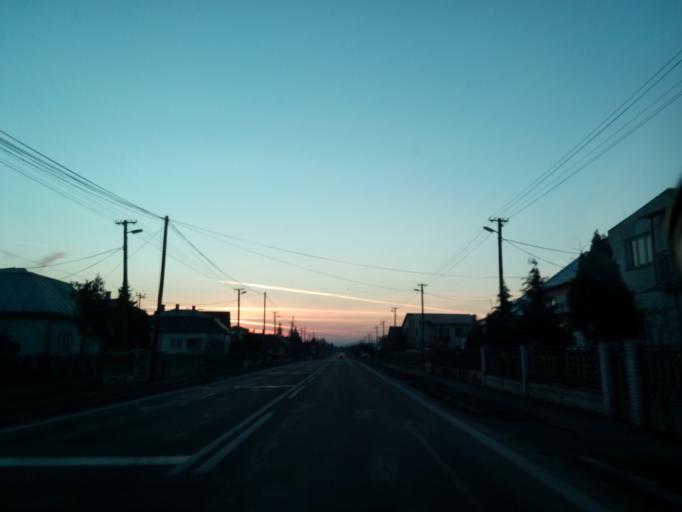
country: SK
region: Kosicky
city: Vinne
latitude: 48.7669
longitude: 22.0415
